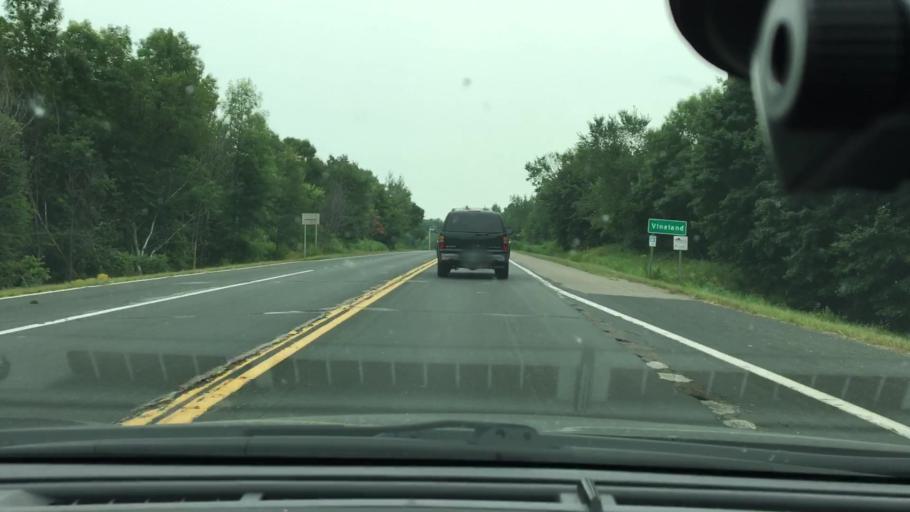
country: US
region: Minnesota
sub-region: Mille Lacs County
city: Vineland
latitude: 46.2059
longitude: -93.7855
